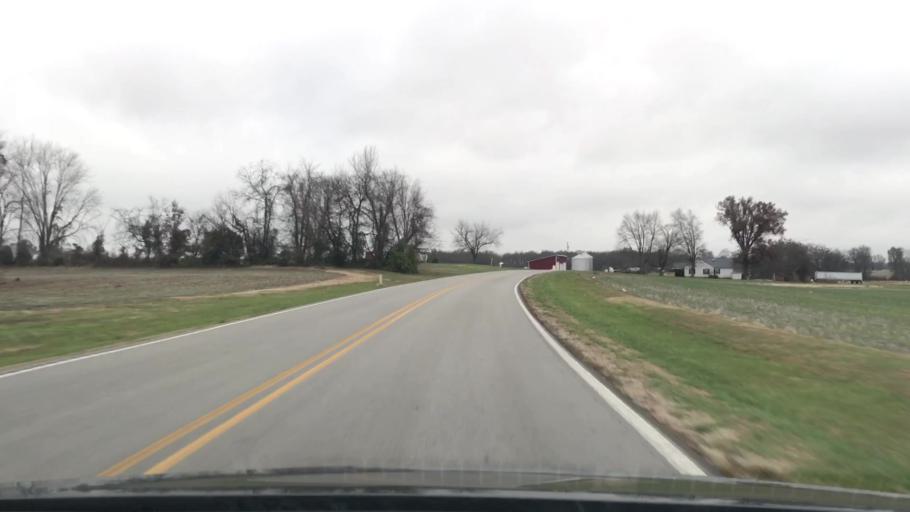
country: US
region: Kentucky
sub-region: Todd County
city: Guthrie
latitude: 36.7308
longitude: -87.1896
